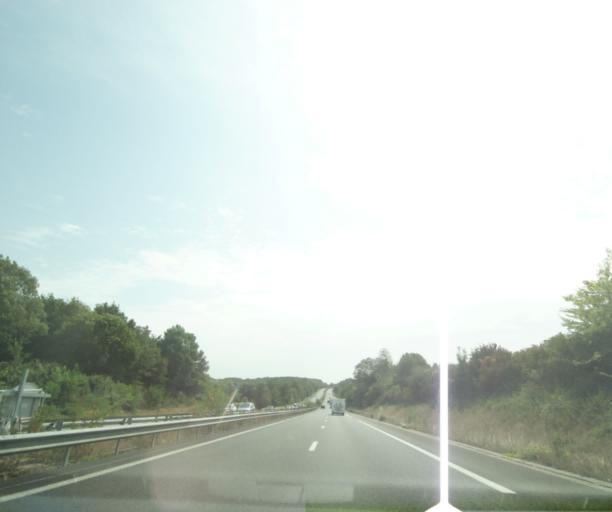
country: FR
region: Poitou-Charentes
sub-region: Departement de la Charente-Maritime
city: Saint-Savinien
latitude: 45.8704
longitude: -0.6227
